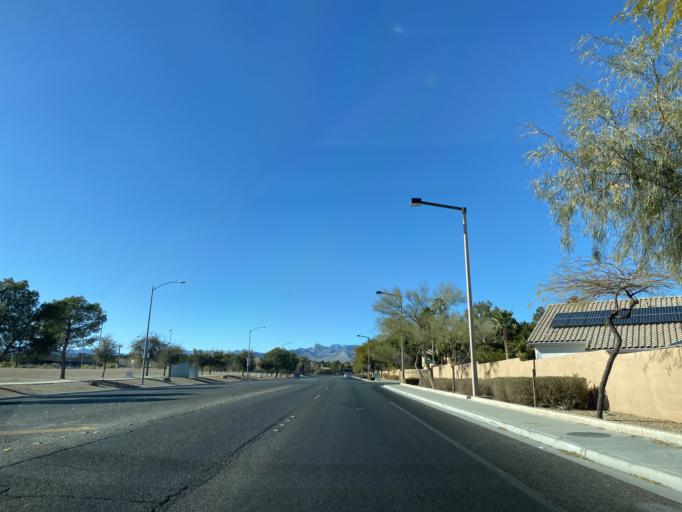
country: US
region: Nevada
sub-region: Clark County
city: Summerlin South
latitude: 36.1887
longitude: -115.2823
